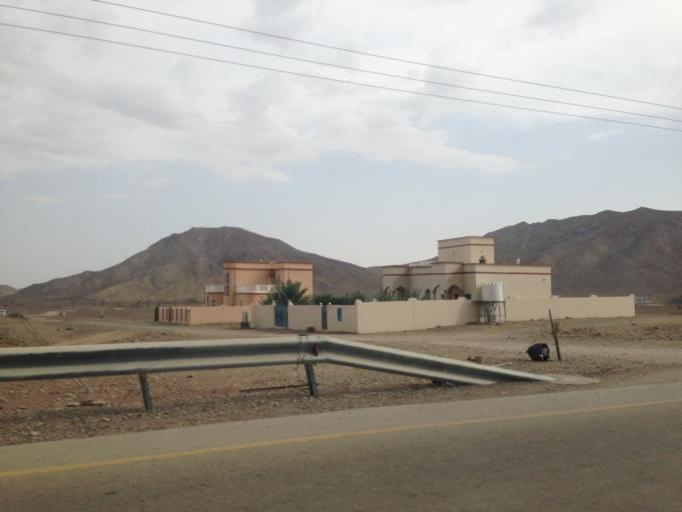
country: OM
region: Ash Sharqiyah
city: Badiyah
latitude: 22.5396
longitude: 58.9853
